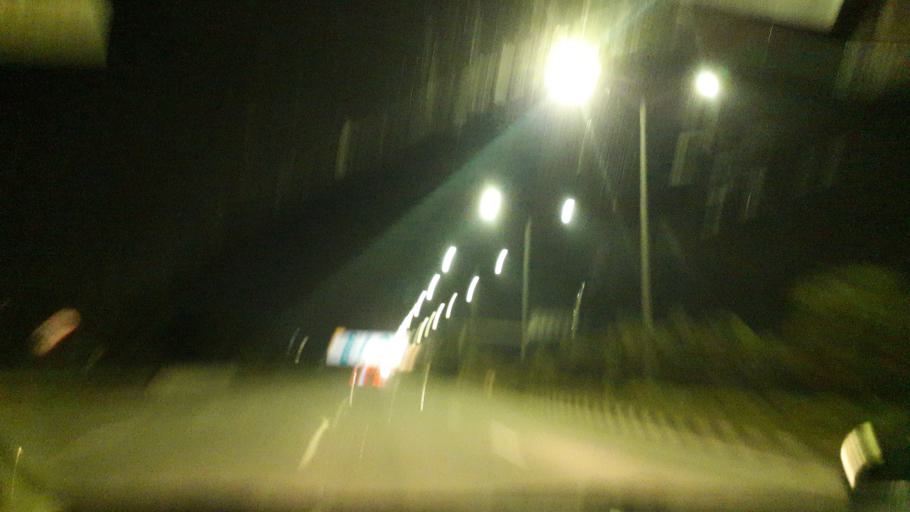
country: IN
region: Telangana
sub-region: Hyderabad
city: Hyderabad
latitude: 17.3354
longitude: 78.3685
